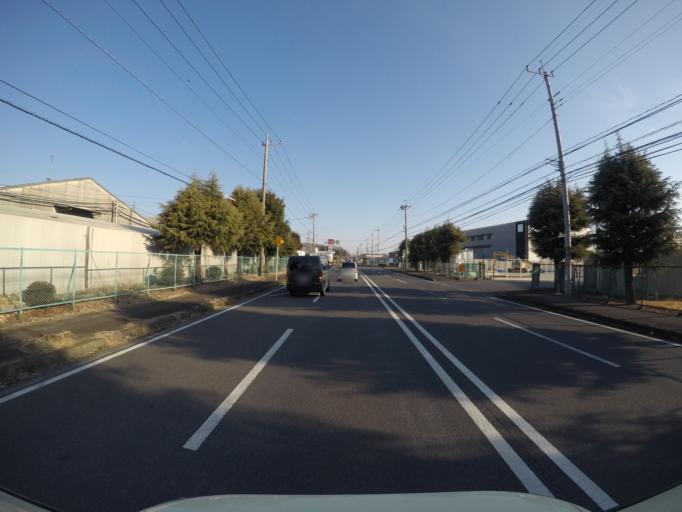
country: JP
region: Tochigi
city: Kaminokawa
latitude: 36.4681
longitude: 139.9660
